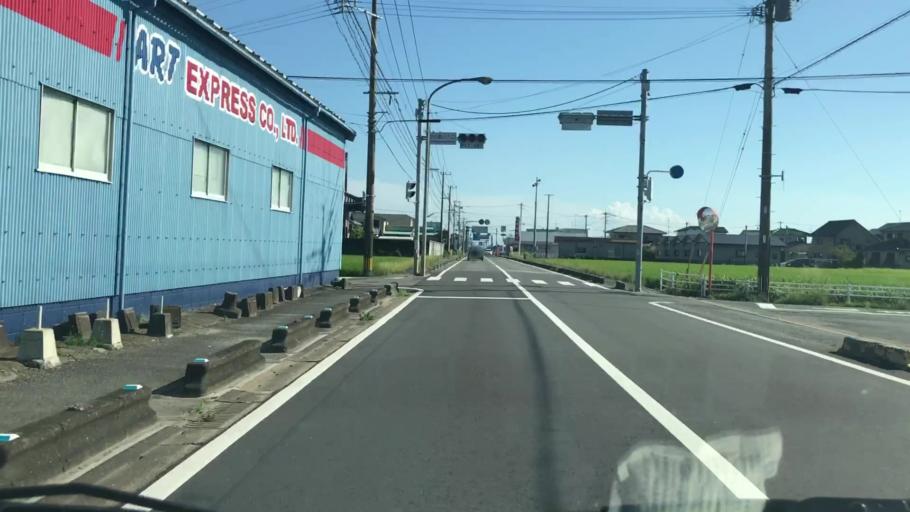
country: JP
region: Saga Prefecture
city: Okawa
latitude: 33.2085
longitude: 130.3354
